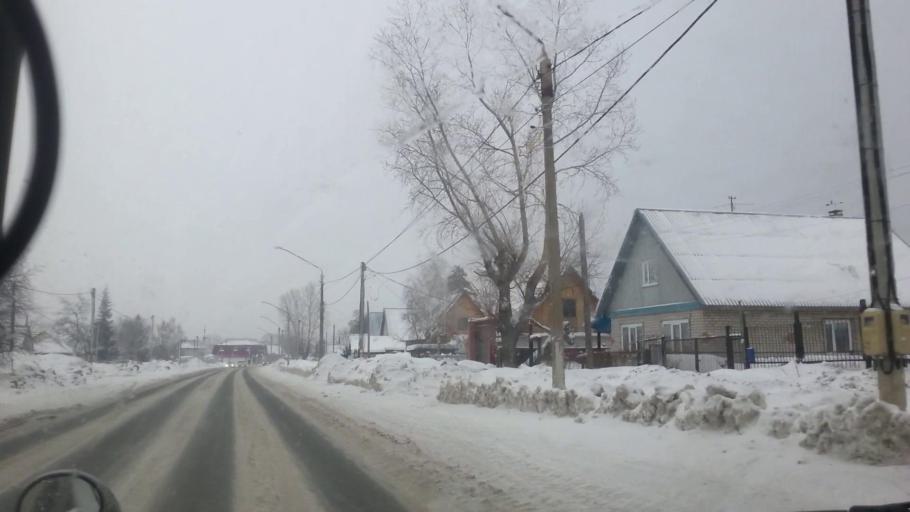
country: RU
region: Altai Krai
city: Vlasikha
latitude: 53.2925
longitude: 83.5695
